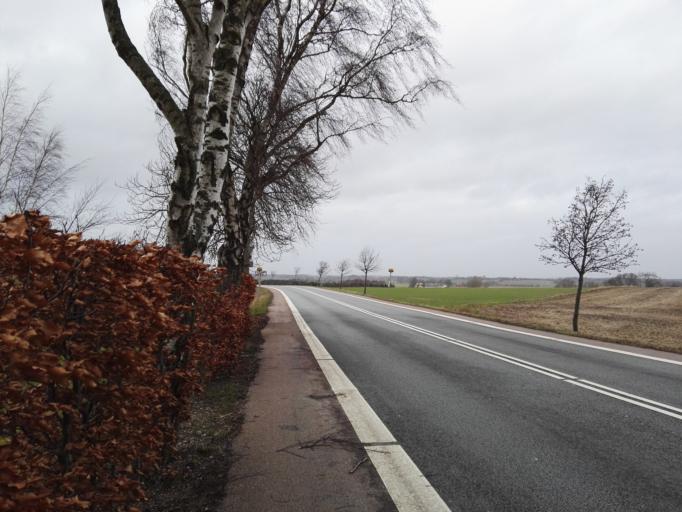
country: DK
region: Capital Region
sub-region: Frederikssund Kommune
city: Skibby
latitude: 55.6758
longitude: 11.9322
